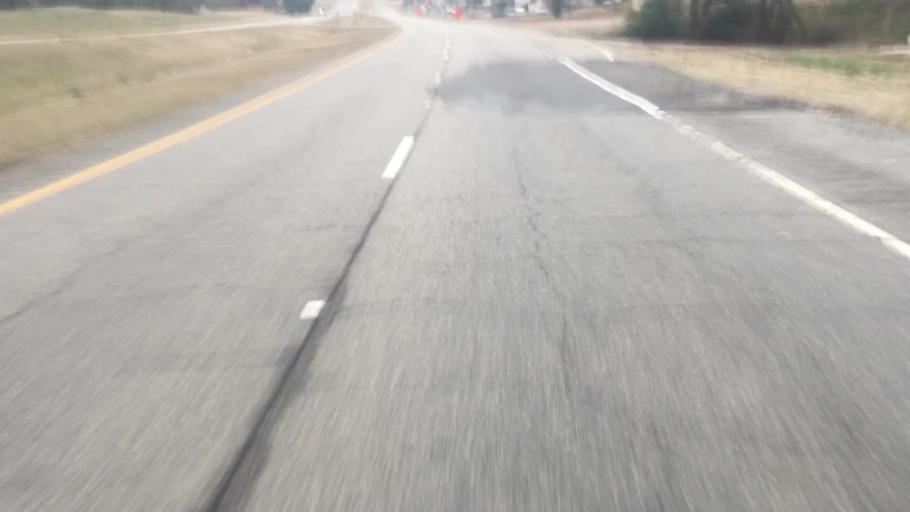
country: US
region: Alabama
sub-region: Walker County
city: Sumiton
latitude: 33.7622
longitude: -87.0683
